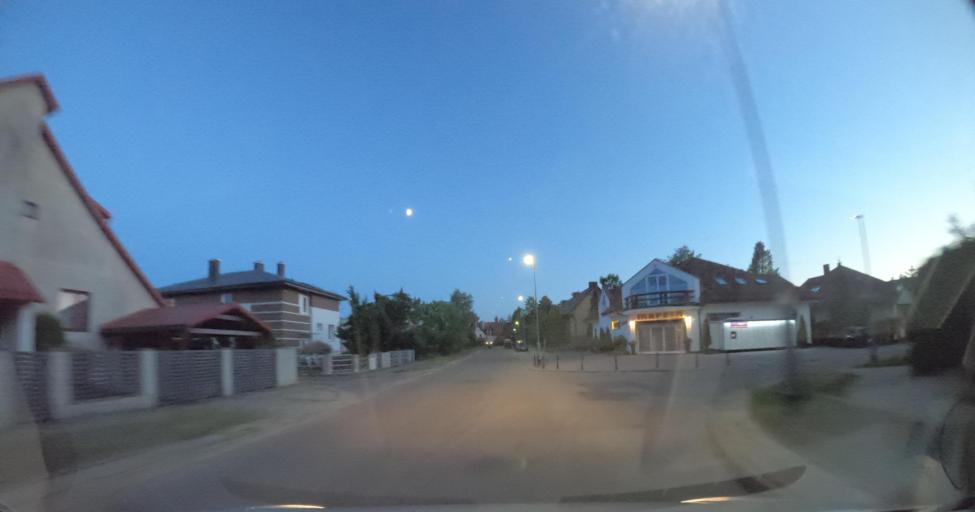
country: PL
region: Pomeranian Voivodeship
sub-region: Gdynia
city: Wielki Kack
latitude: 54.4278
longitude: 18.4668
